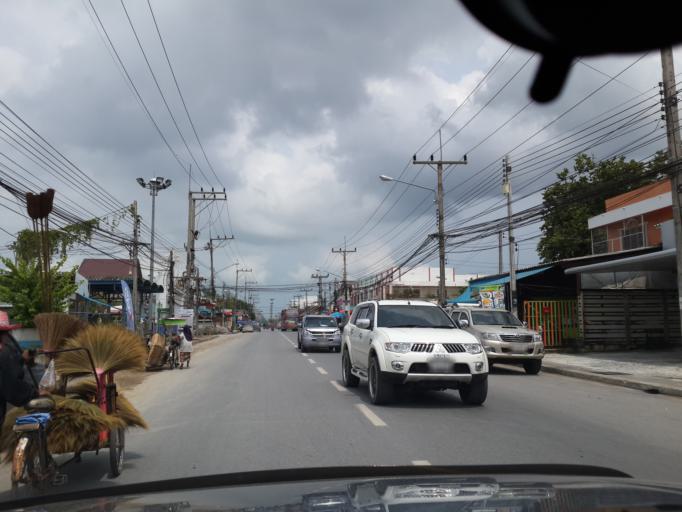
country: TH
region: Pattani
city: Pattani
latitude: 6.8550
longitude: 101.2529
